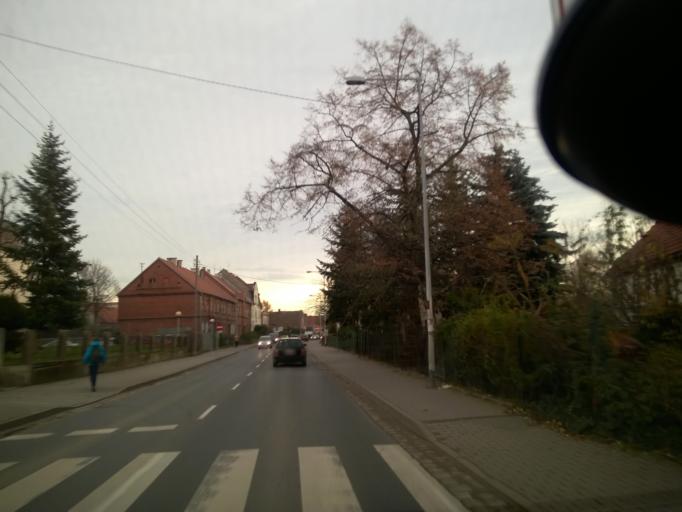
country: PL
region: Lower Silesian Voivodeship
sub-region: Powiat wroclawski
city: Smolec
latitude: 51.0985
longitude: 16.9432
